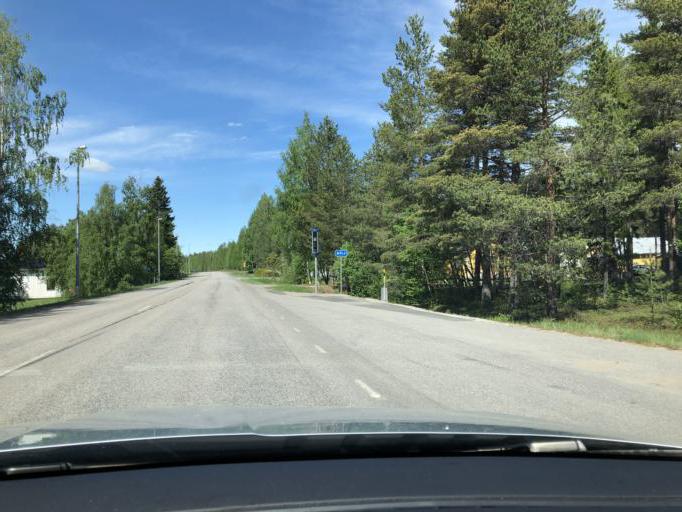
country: SE
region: Norrbotten
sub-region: Pitea Kommun
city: Bergsviken
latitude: 65.3803
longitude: 21.3403
